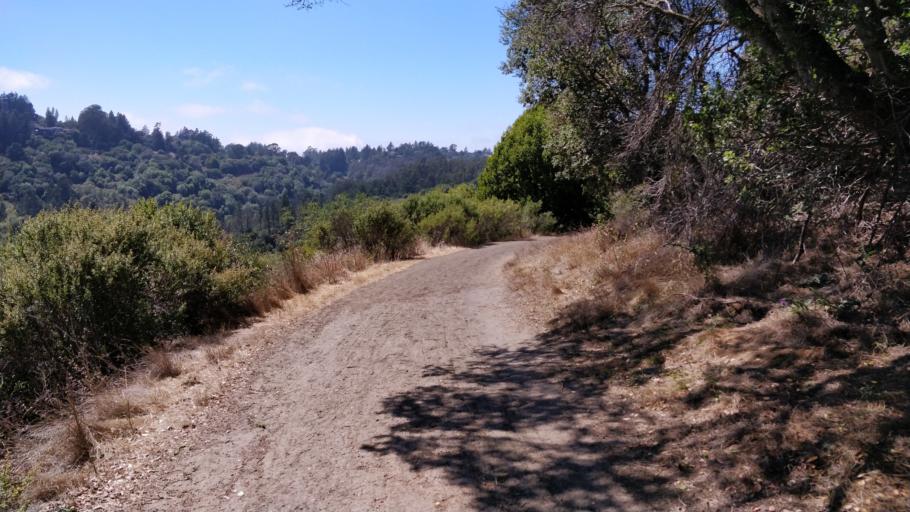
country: US
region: California
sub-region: Contra Costa County
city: Kensington
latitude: 37.9067
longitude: -122.2531
